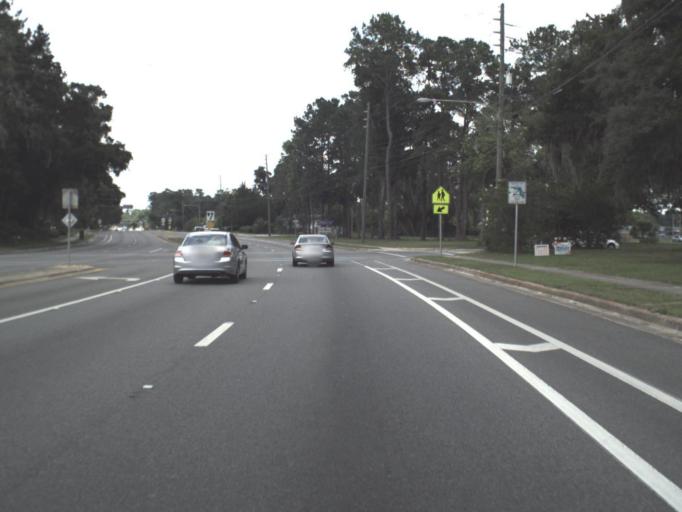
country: US
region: Florida
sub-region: Alachua County
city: Gainesville
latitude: 29.6405
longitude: -82.3116
